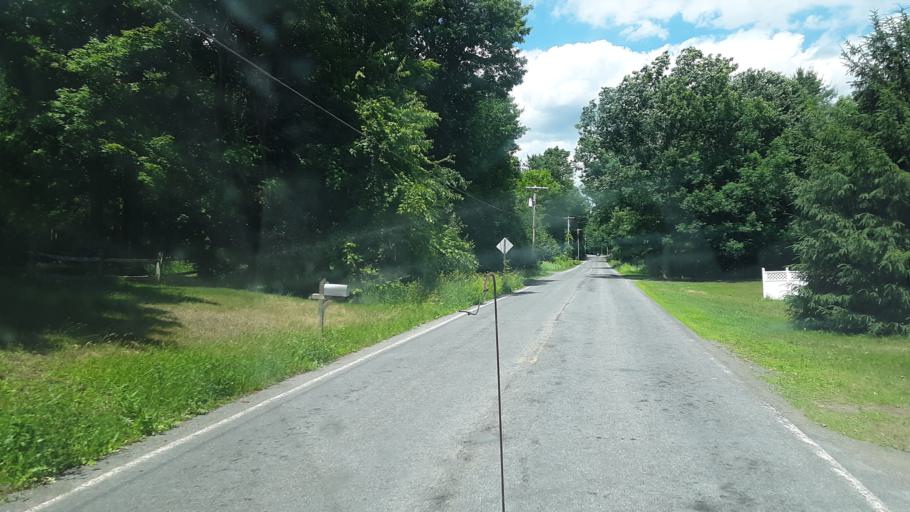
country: US
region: New York
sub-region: Oneida County
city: Rome
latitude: 43.2267
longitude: -75.5954
